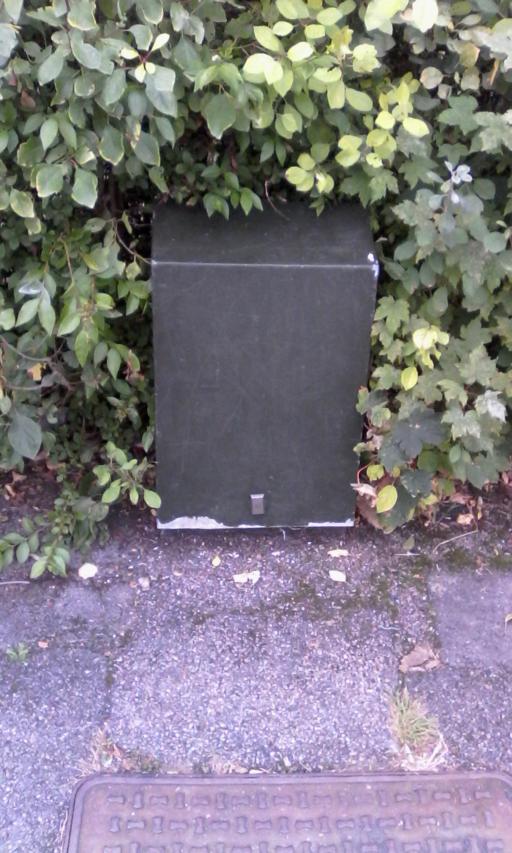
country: GB
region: England
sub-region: Hertfordshire
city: Ware
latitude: 51.8164
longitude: -0.0216
